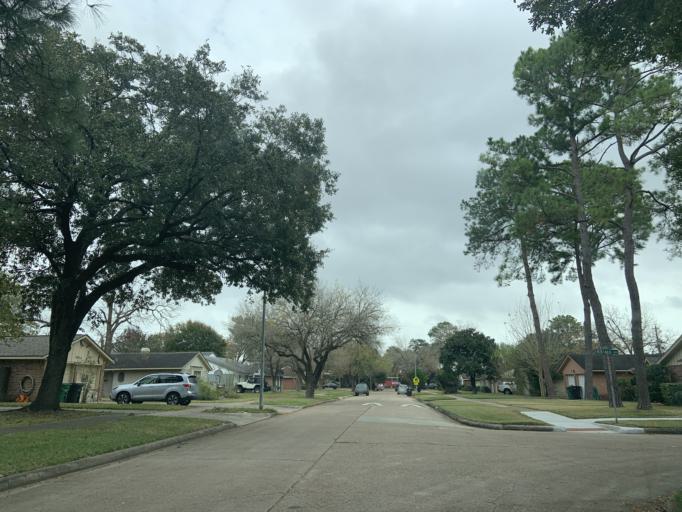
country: US
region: Texas
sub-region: Harris County
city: Bellaire
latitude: 29.6875
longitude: -95.5161
